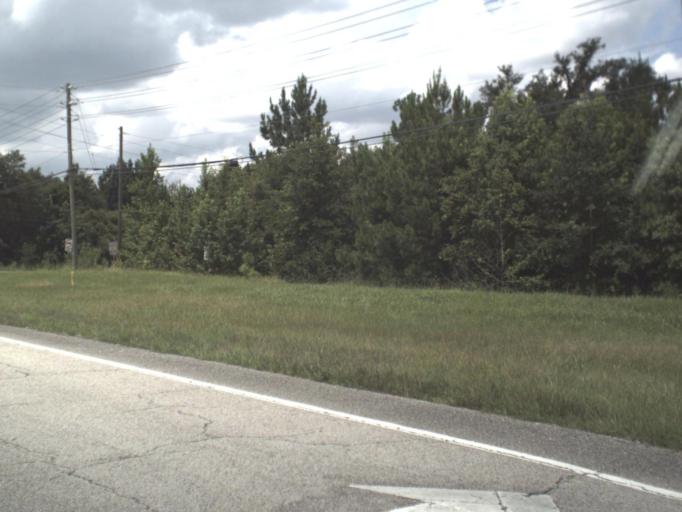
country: US
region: Florida
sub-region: Hernando County
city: South Brooksville
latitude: 28.4926
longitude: -82.4288
